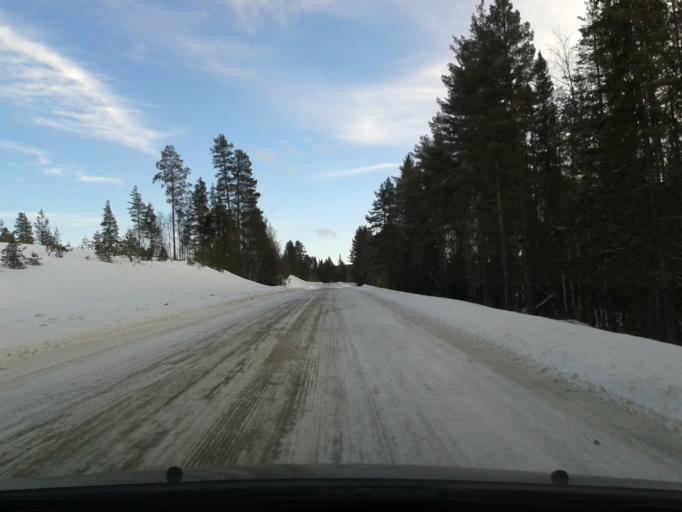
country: SE
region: Vaesterbotten
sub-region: Asele Kommun
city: Asele
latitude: 64.2451
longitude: 17.2885
